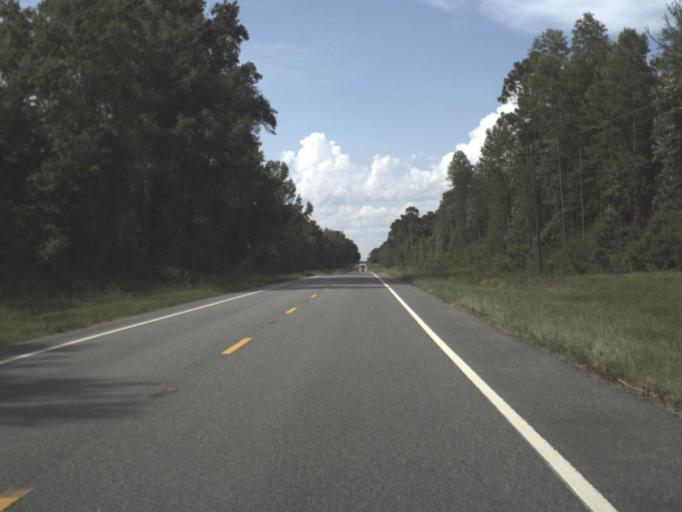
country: US
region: Florida
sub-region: Taylor County
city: Perry
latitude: 30.2405
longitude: -83.6198
